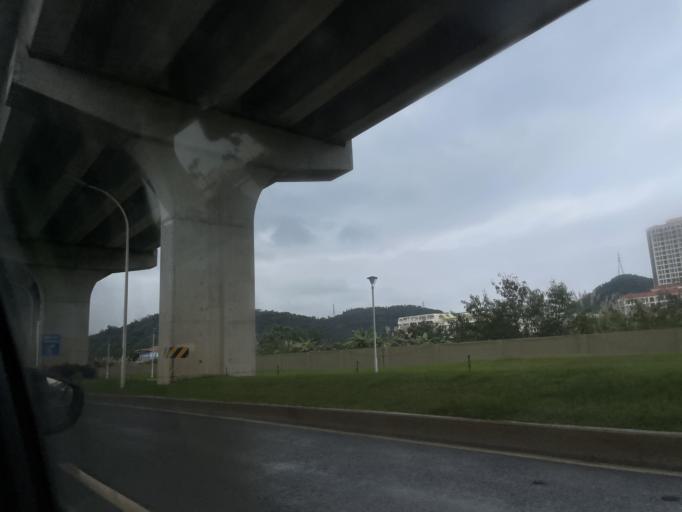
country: CN
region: Guangdong
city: Wanzai
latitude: 22.1765
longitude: 113.4879
